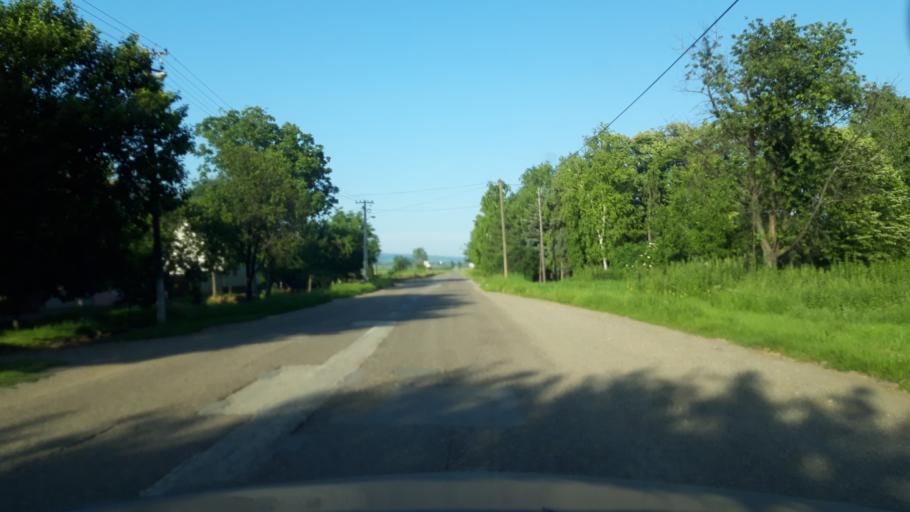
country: HR
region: Vukovarsko-Srijemska
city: Ilok
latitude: 45.1012
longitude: 19.4552
